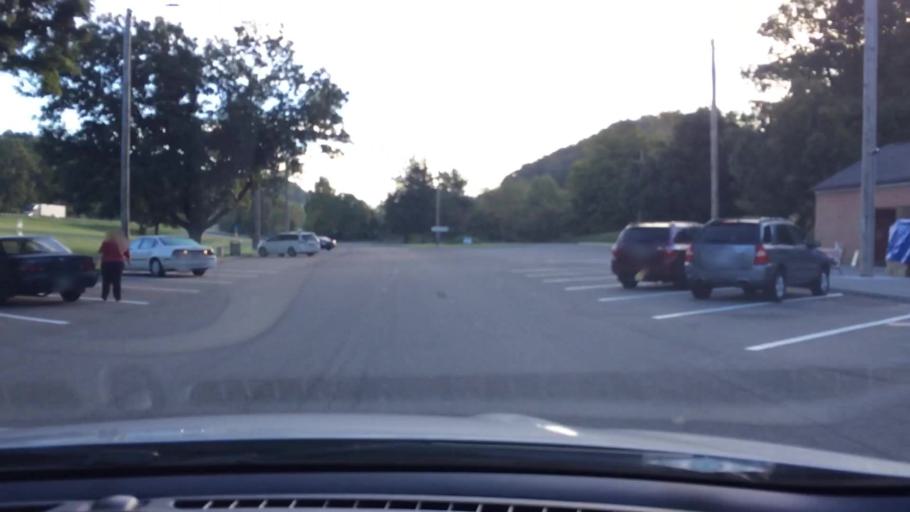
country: US
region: Tennessee
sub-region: Sullivan County
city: Walnut Hill
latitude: 36.5965
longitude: -82.2398
